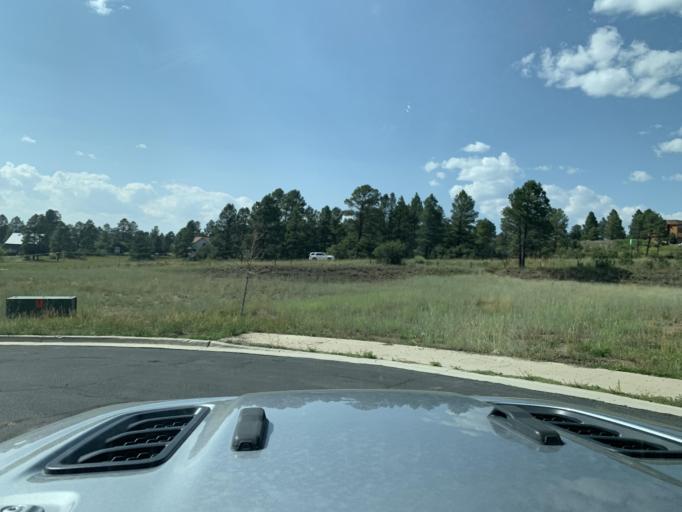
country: US
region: Colorado
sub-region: Archuleta County
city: Pagosa Springs
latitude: 37.2654
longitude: -107.0554
